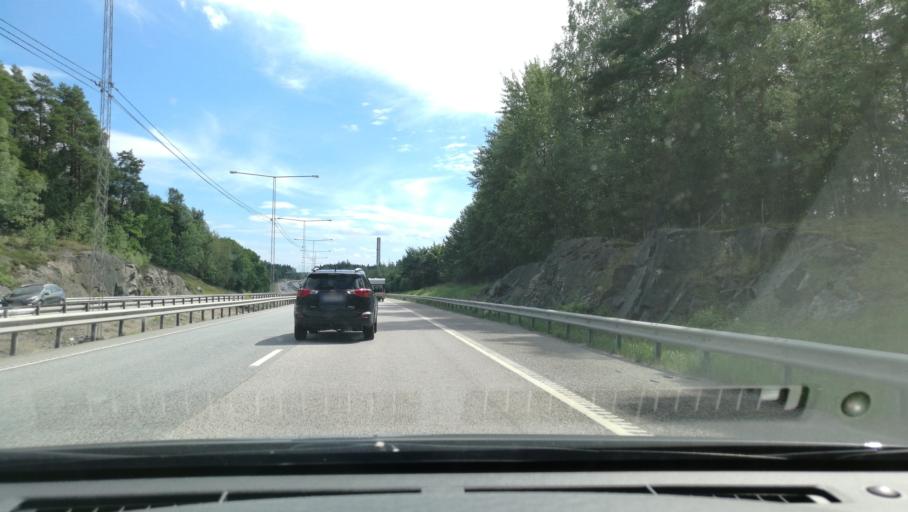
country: SE
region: Stockholm
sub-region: Jarfalla Kommun
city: Jakobsberg
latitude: 59.4360
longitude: 17.8443
